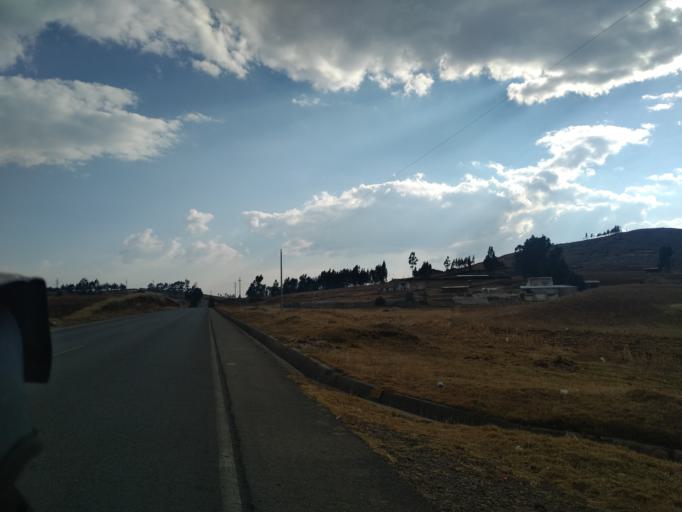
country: PE
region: Cajamarca
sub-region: Provincia de Cajamarca
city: Encanada
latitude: -7.1417
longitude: -78.3905
